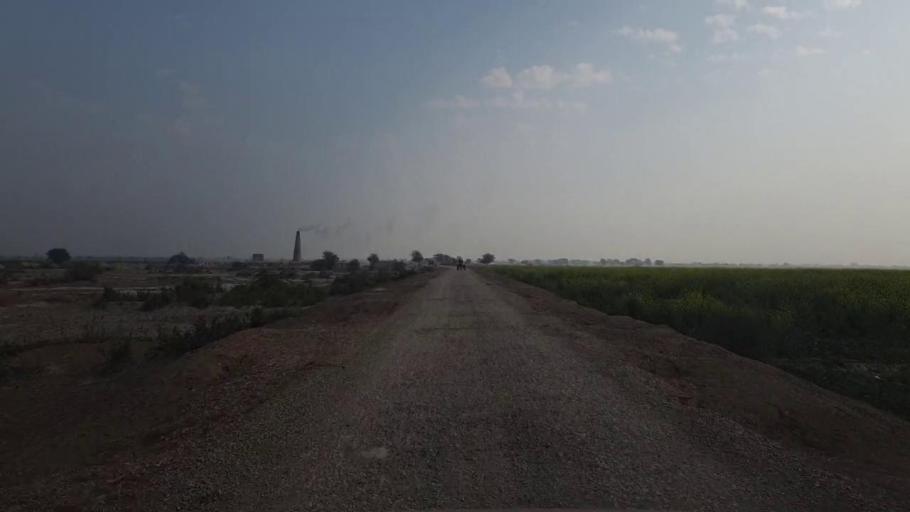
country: PK
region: Sindh
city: Hala
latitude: 25.7650
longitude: 68.4159
